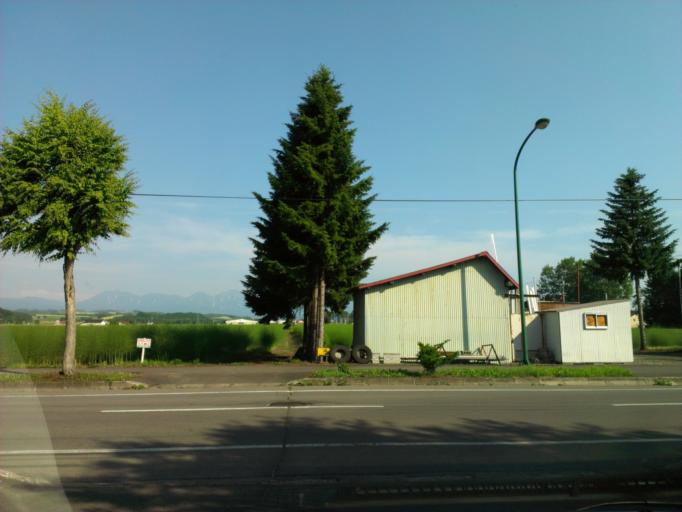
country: JP
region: Hokkaido
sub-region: Asahikawa-shi
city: Asahikawa
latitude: 43.5877
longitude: 142.4768
